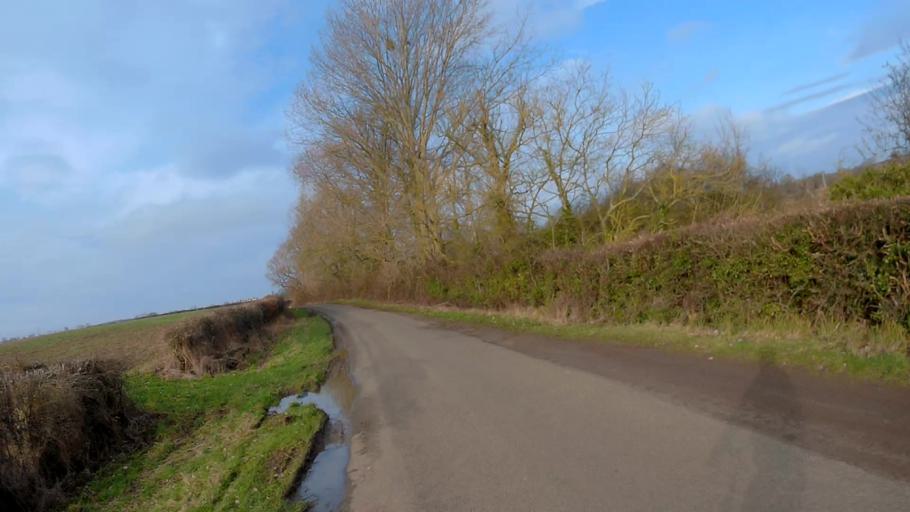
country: GB
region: England
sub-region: Lincolnshire
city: Bourne
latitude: 52.7715
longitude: -0.4247
